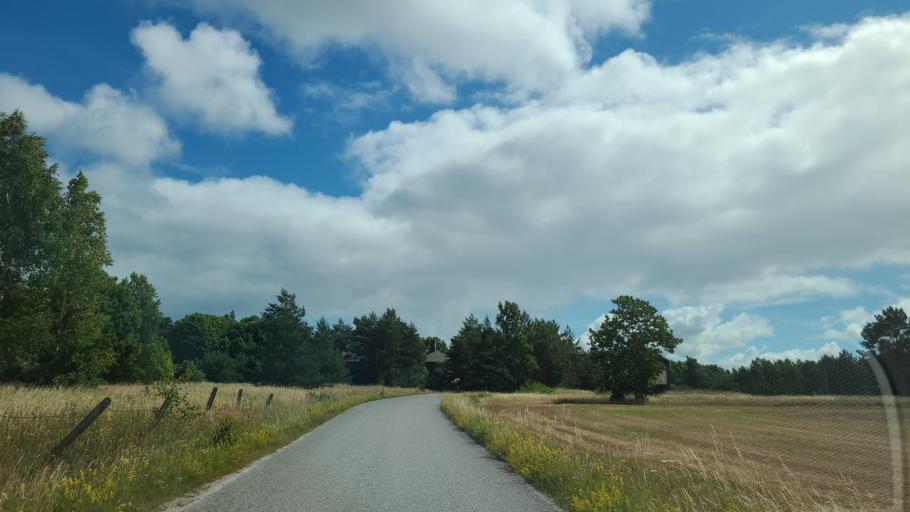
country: FI
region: Varsinais-Suomi
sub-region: Aboland-Turunmaa
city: Nagu
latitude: 60.1701
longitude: 22.0461
